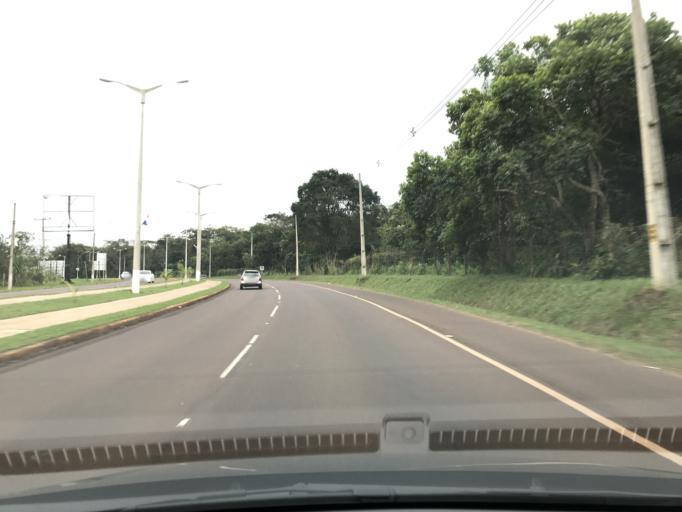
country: PY
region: Canindeyu
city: Salto del Guaira
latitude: -24.0377
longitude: -54.3130
